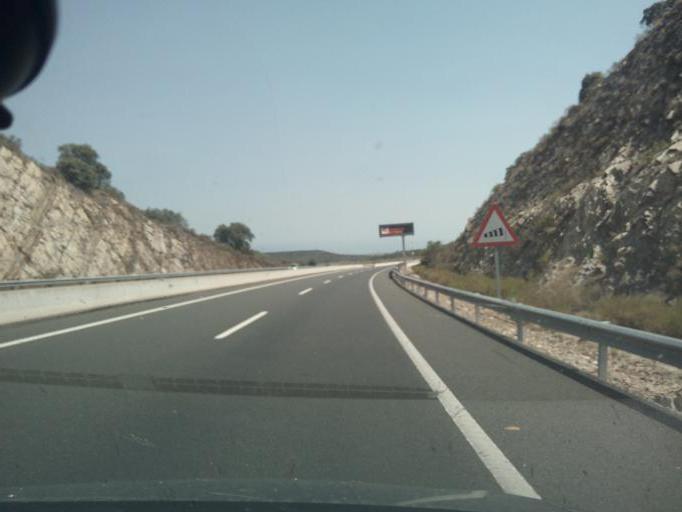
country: ES
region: Extremadura
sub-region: Provincia de Caceres
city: Romangordo
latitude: 39.7769
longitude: -5.7366
